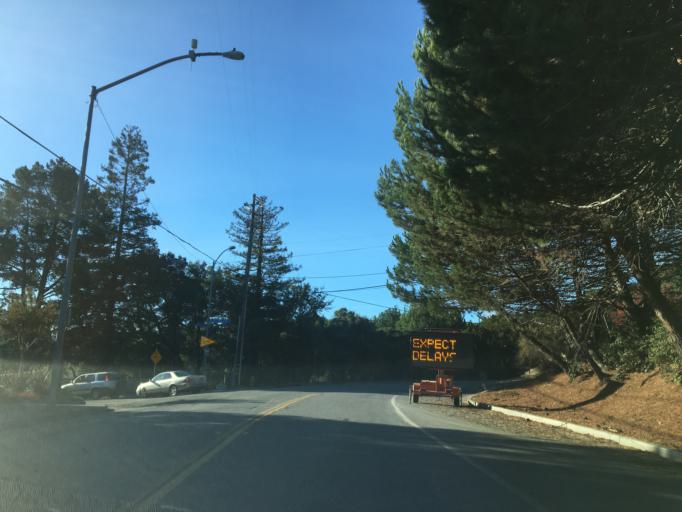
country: US
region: California
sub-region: Santa Clara County
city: Cupertino
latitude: 37.3111
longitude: -122.0695
